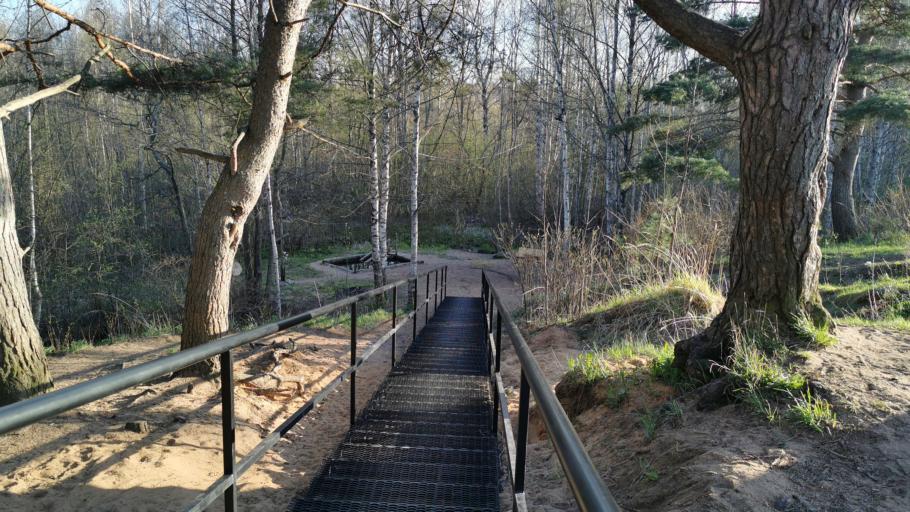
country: RU
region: St.-Petersburg
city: Bol'shaya Izhora
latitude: 59.9341
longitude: 29.5589
